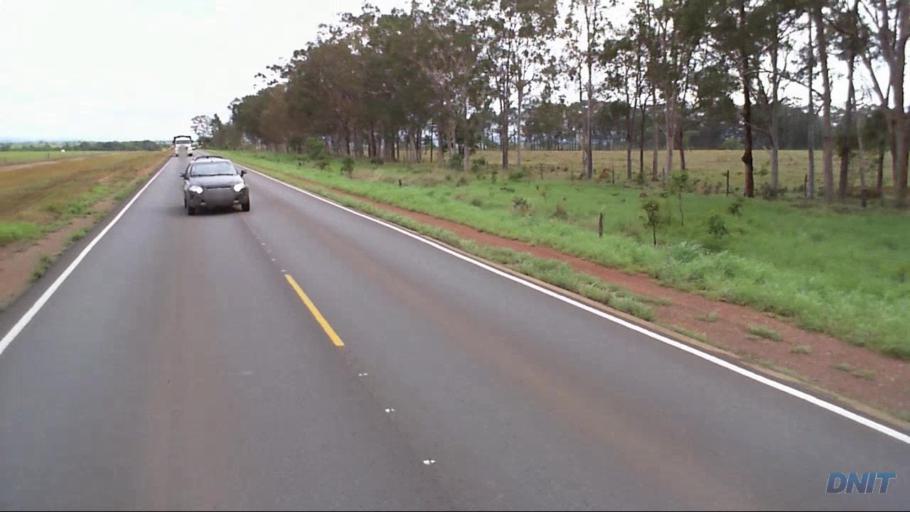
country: BR
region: Goias
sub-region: Padre Bernardo
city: Padre Bernardo
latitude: -15.3233
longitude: -48.2304
